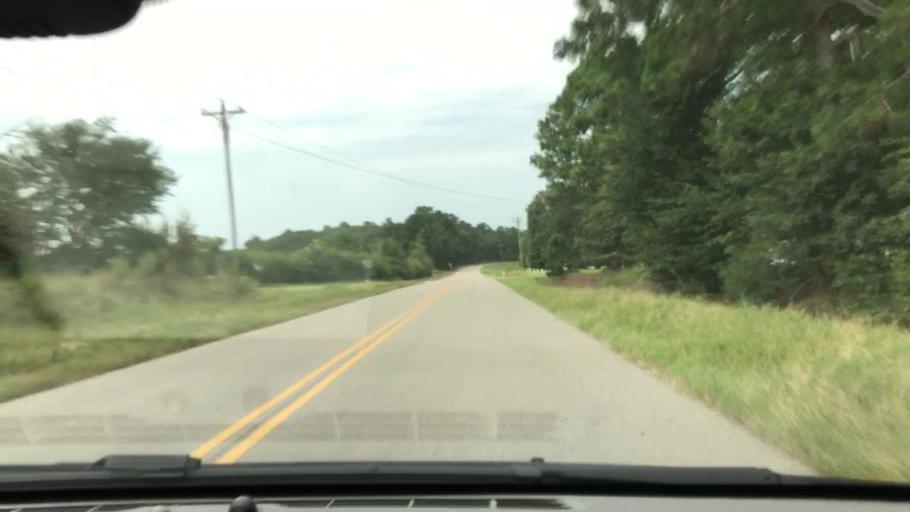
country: US
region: Alabama
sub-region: Houston County
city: Ashford
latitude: 31.2209
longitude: -85.1874
